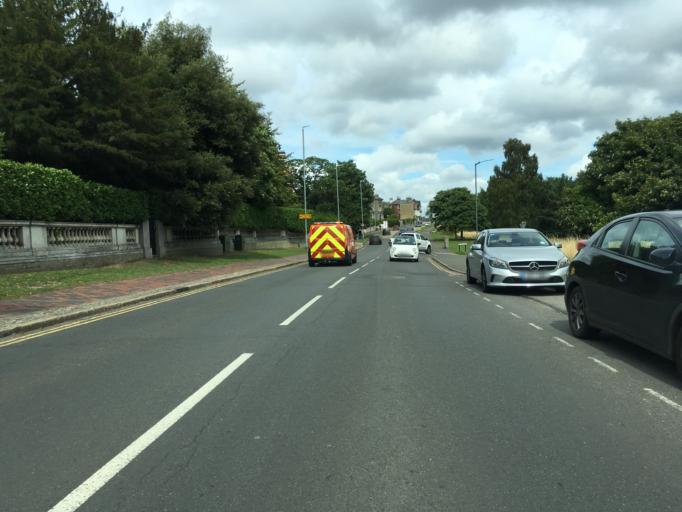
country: GB
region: England
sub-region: Kent
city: Royal Tunbridge Wells
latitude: 51.1320
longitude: 0.2549
